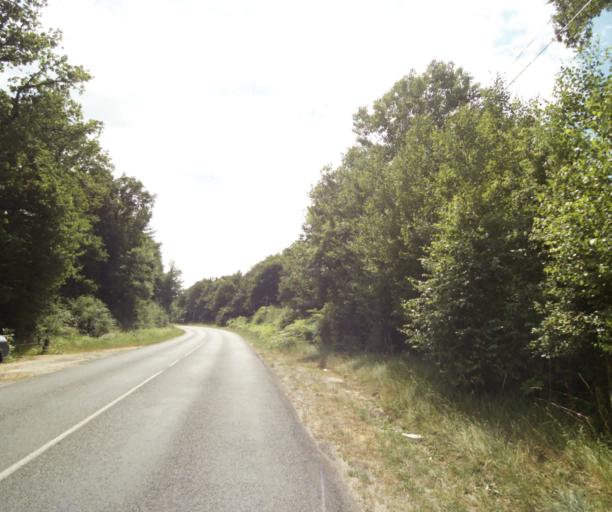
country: FR
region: Ile-de-France
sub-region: Departement de Seine-et-Marne
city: Dammarie-les-Lys
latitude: 48.4911
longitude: 2.6304
